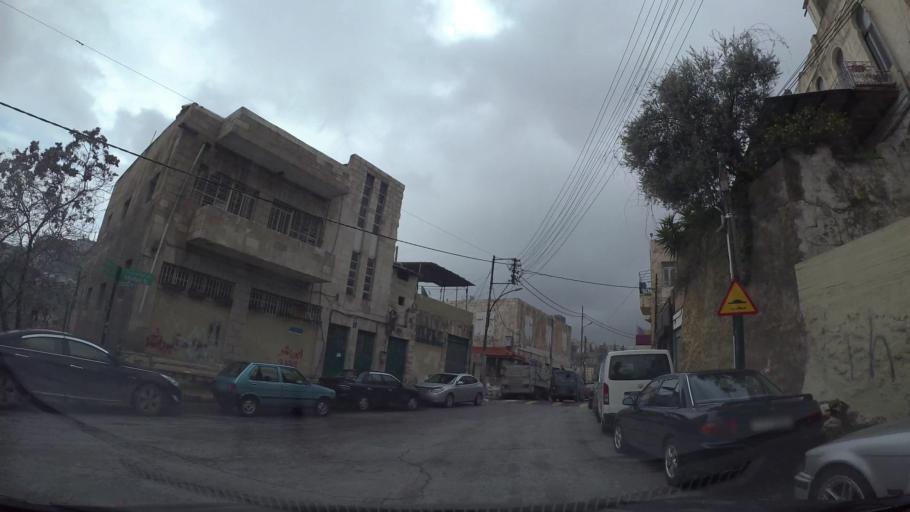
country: JO
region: Amman
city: Amman
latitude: 31.9487
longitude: 35.9327
